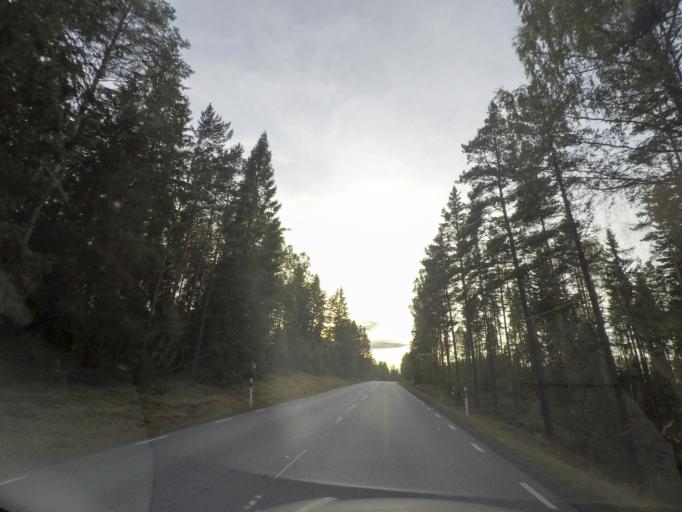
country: SE
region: OErebro
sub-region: Nora Kommun
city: As
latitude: 59.5235
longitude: 14.8357
